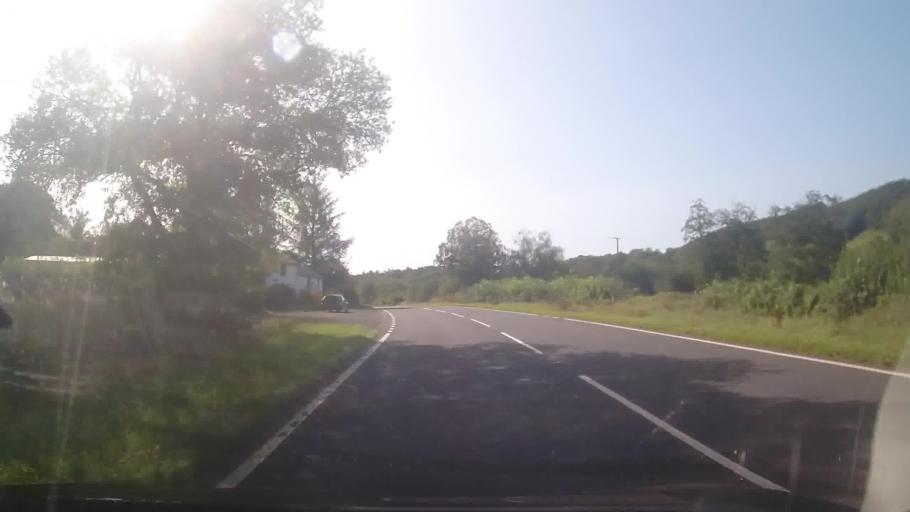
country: GB
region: Wales
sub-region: Sir Powys
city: Rhayader
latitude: 52.1280
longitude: -3.6151
